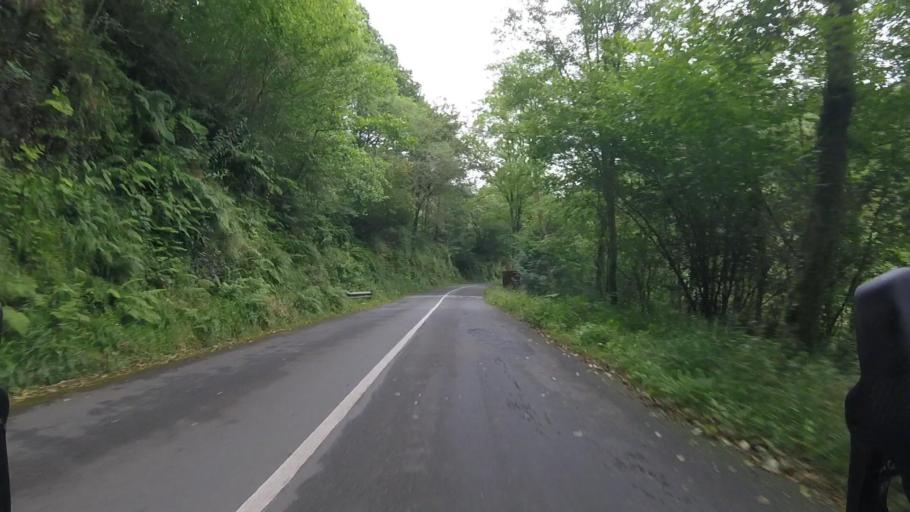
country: ES
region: Basque Country
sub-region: Provincia de Guipuzcoa
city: Irun
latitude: 43.2828
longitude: -1.8221
